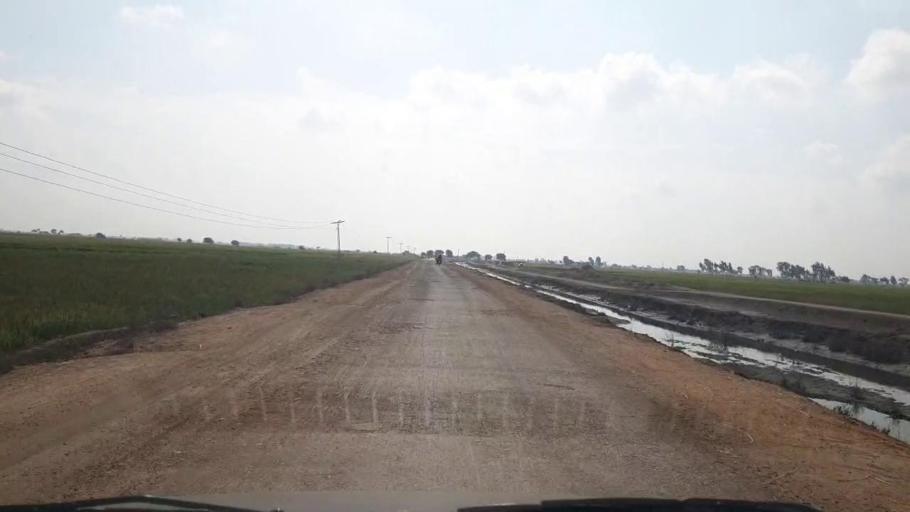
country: PK
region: Sindh
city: Kario
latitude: 24.6226
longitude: 68.5554
